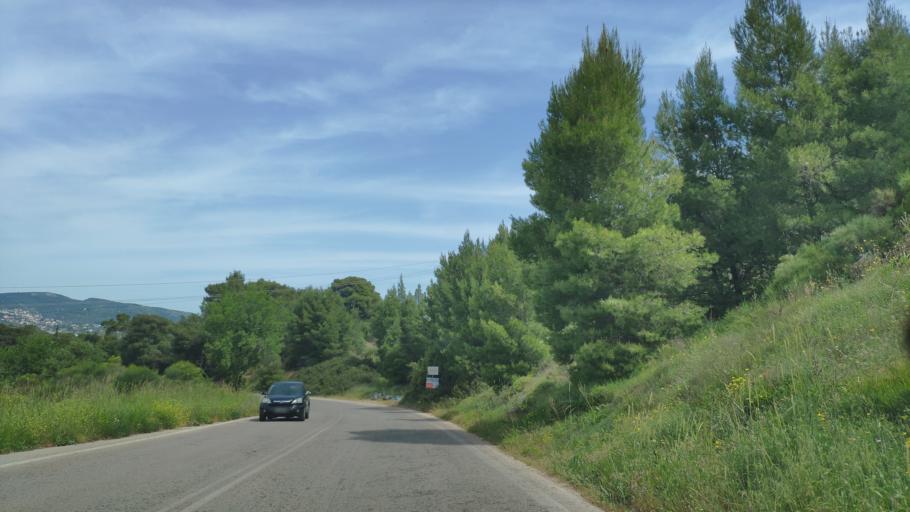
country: GR
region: Attica
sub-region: Nomarchia Anatolikis Attikis
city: Agios Stefanos
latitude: 38.1624
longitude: 23.8618
